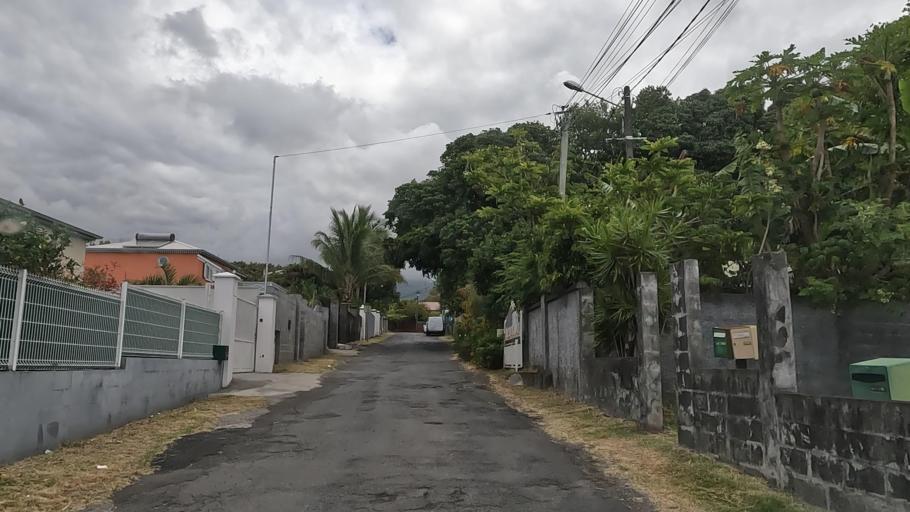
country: RE
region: Reunion
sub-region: Reunion
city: Saint-Benoit
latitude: -21.0907
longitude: 55.7456
